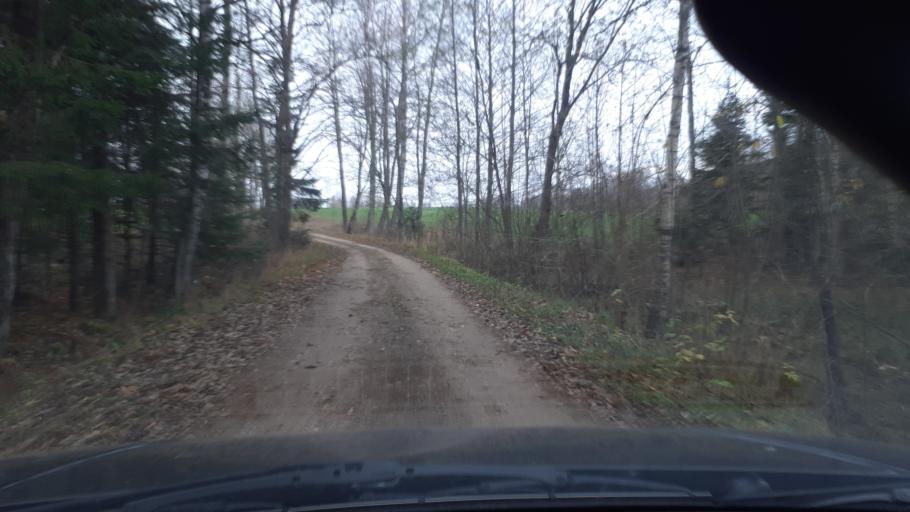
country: LV
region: Alsunga
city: Alsunga
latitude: 56.9429
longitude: 21.6455
